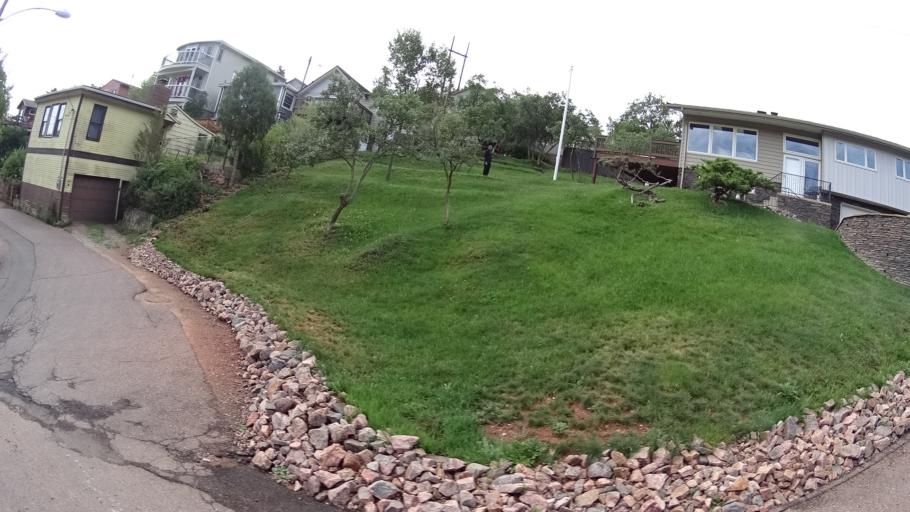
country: US
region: Colorado
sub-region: El Paso County
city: Manitou Springs
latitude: 38.8539
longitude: -104.9132
